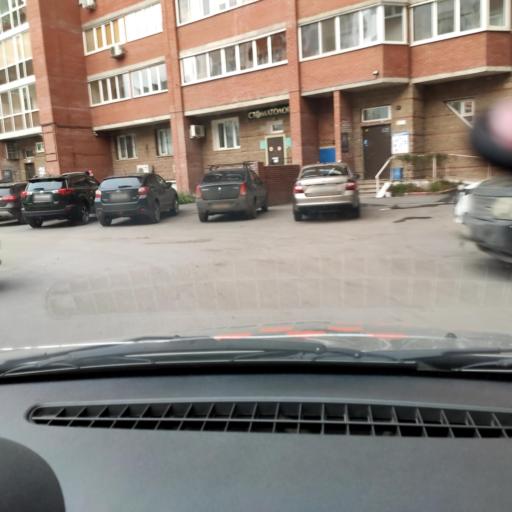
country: RU
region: Bashkortostan
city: Ufa
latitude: 54.7126
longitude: 55.9968
